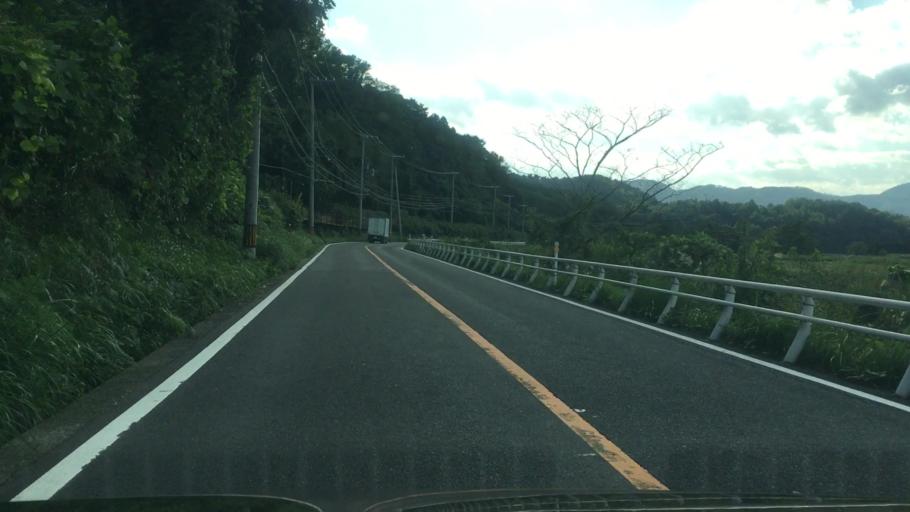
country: JP
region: Hyogo
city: Toyooka
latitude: 35.6067
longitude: 134.9175
